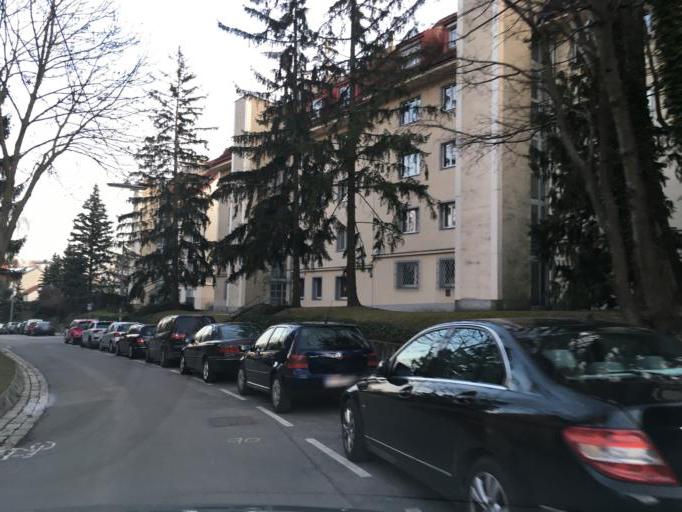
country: AT
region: Vienna
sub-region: Wien Stadt
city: Vienna
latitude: 48.2150
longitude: 16.2919
